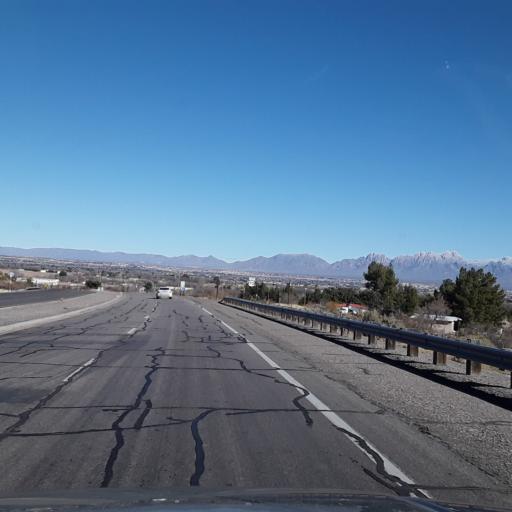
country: US
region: New Mexico
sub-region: Dona Ana County
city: Mesilla
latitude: 32.2940
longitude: -106.8600
